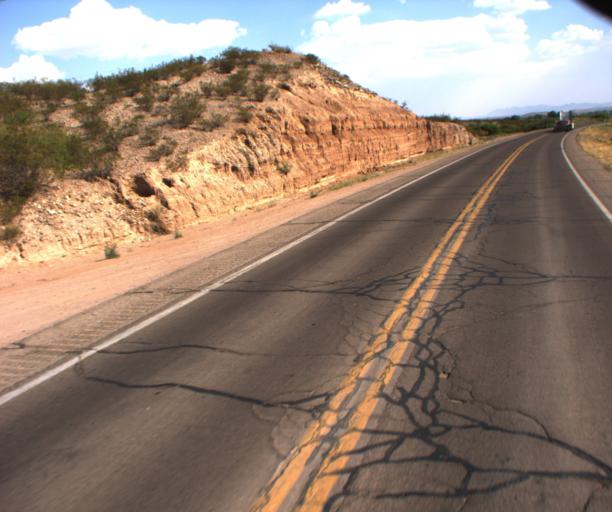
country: US
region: Arizona
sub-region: Greenlee County
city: Clifton
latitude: 32.7345
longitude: -109.0924
